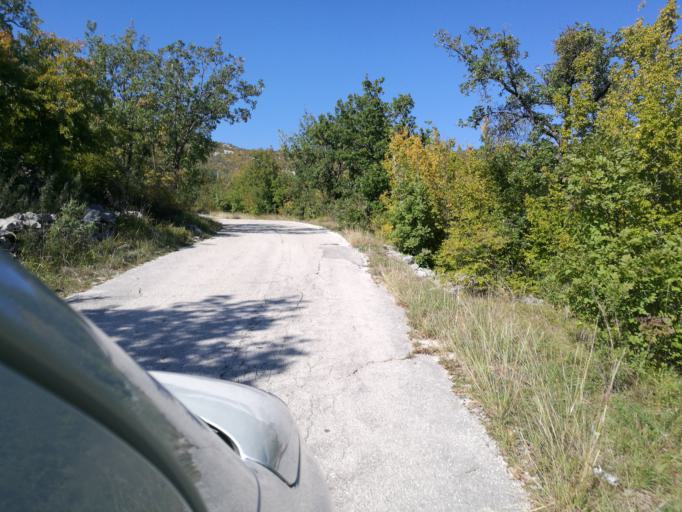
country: HR
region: Splitsko-Dalmatinska
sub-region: Grad Omis
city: Omis
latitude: 43.5145
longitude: 16.7301
